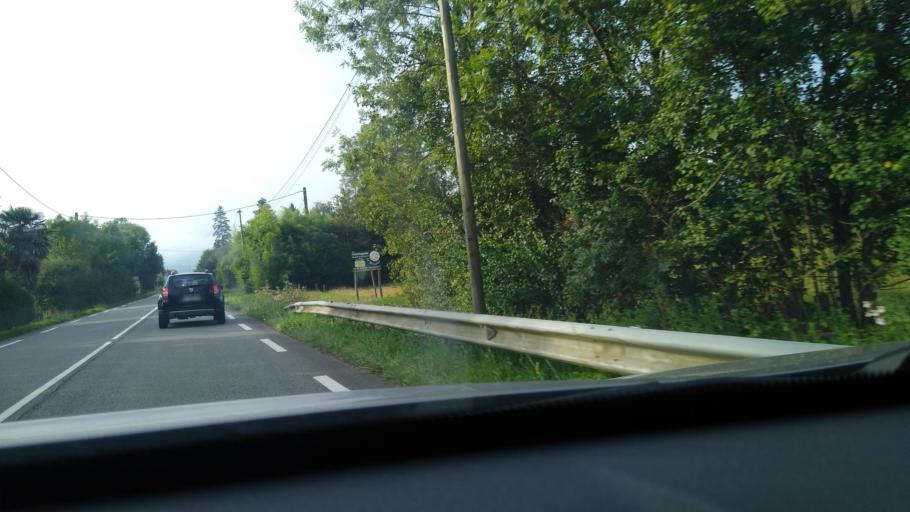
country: FR
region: Midi-Pyrenees
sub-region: Departement de la Haute-Garonne
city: Salies-du-Salat
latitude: 43.0576
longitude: 0.9770
